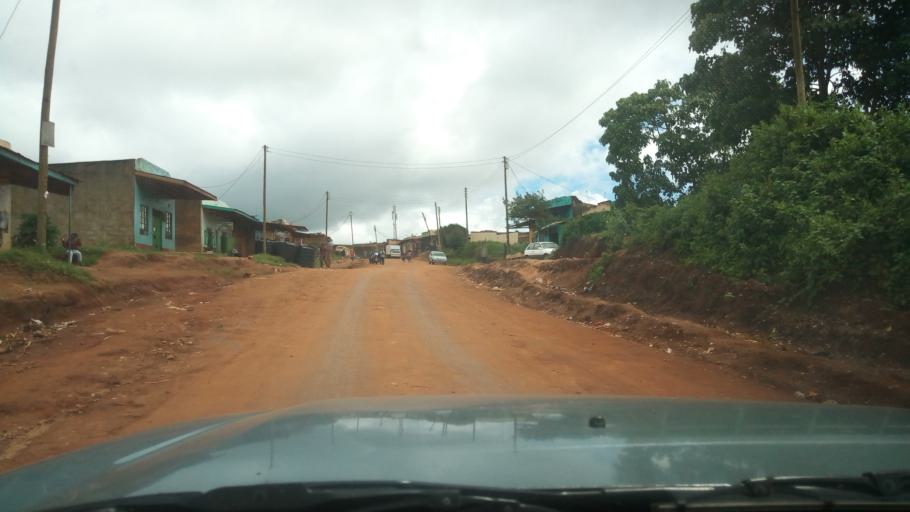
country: KE
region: Makueni
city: Wote
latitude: -1.6644
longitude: 37.4482
